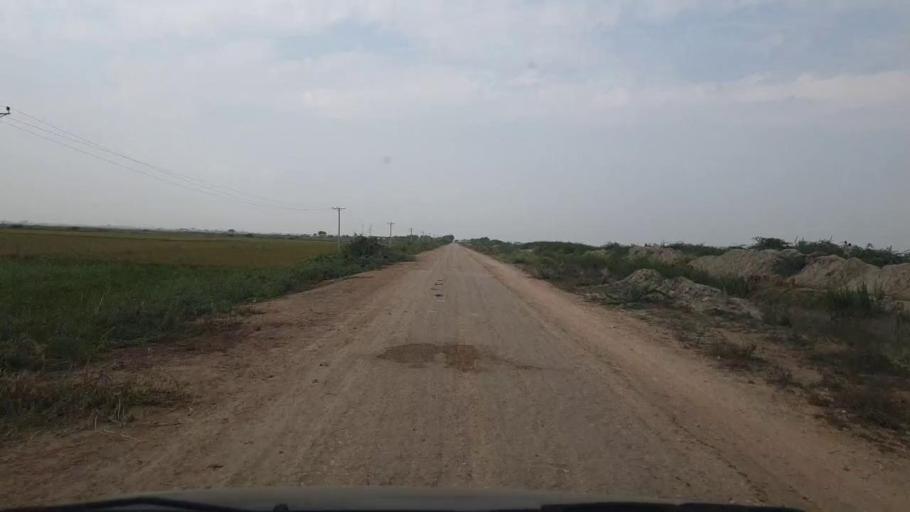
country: PK
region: Sindh
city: Kario
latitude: 24.6171
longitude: 68.5859
